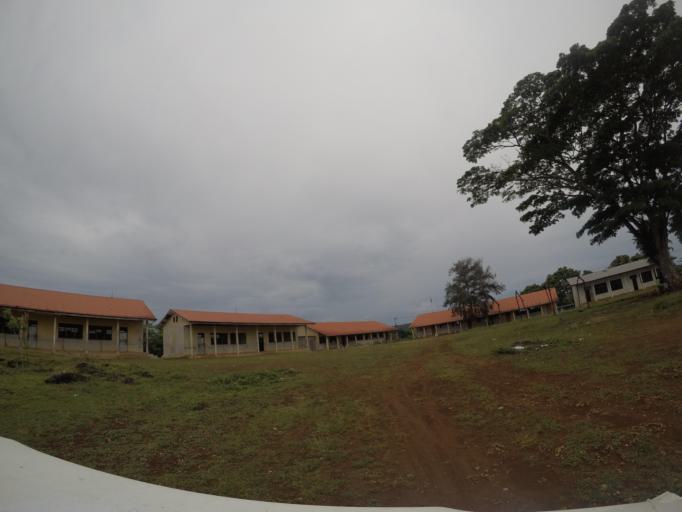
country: TL
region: Lautem
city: Lospalos
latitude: -8.5351
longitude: 126.9995
